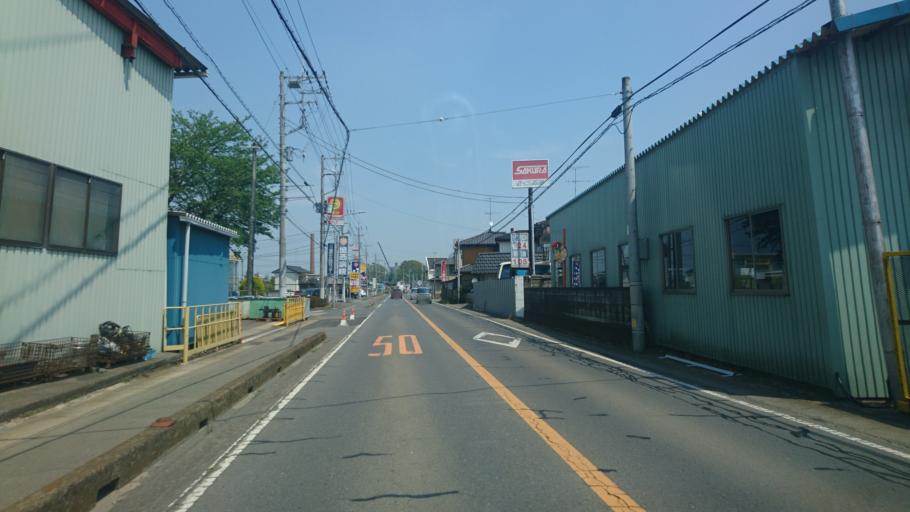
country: JP
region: Ibaraki
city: Yuki
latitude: 36.3048
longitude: 139.8508
